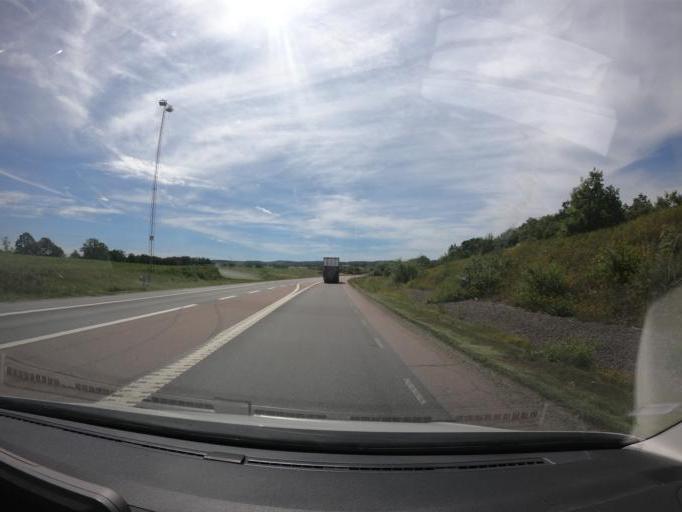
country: SE
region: Skane
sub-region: Klippans Kommun
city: Klippan
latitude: 56.1300
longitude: 13.1099
